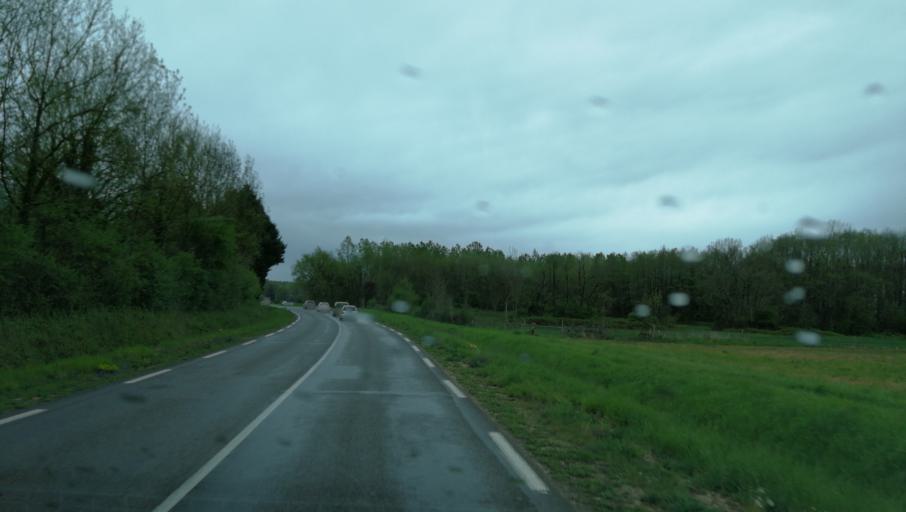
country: FR
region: Franche-Comte
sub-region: Departement du Jura
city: Bletterans
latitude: 46.7153
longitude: 5.4751
